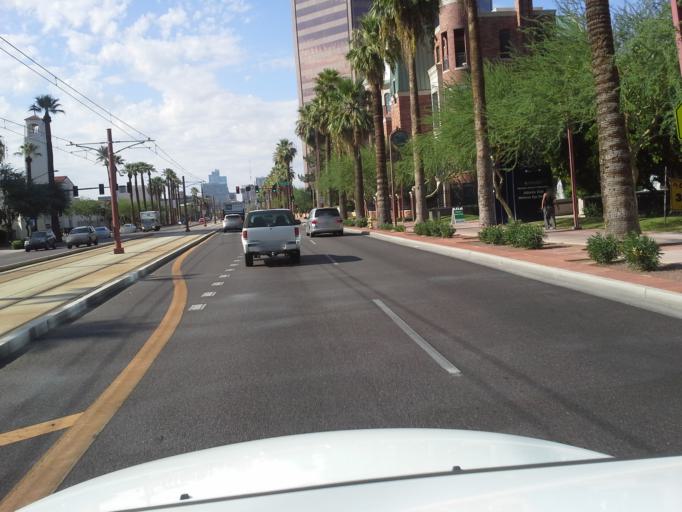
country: US
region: Arizona
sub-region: Maricopa County
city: Phoenix
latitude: 33.4704
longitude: -112.0739
